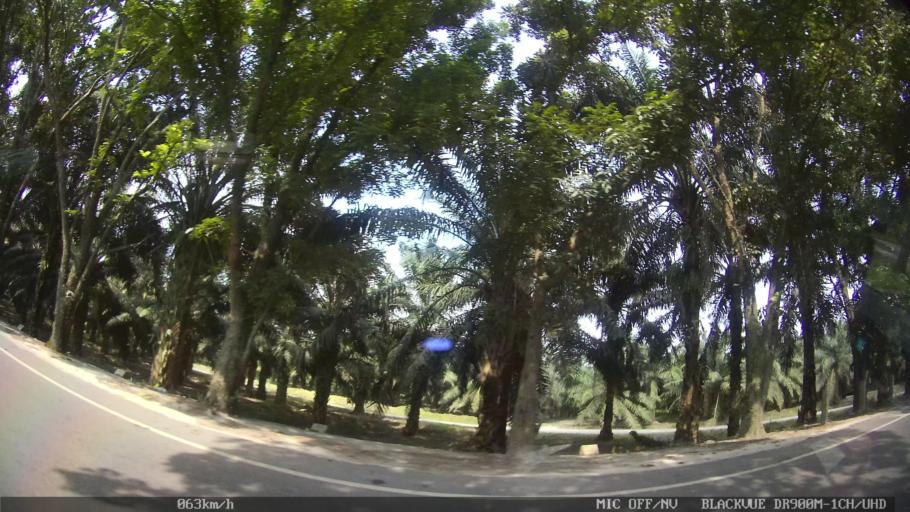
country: ID
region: North Sumatra
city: Binjai
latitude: 3.6514
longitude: 98.5340
